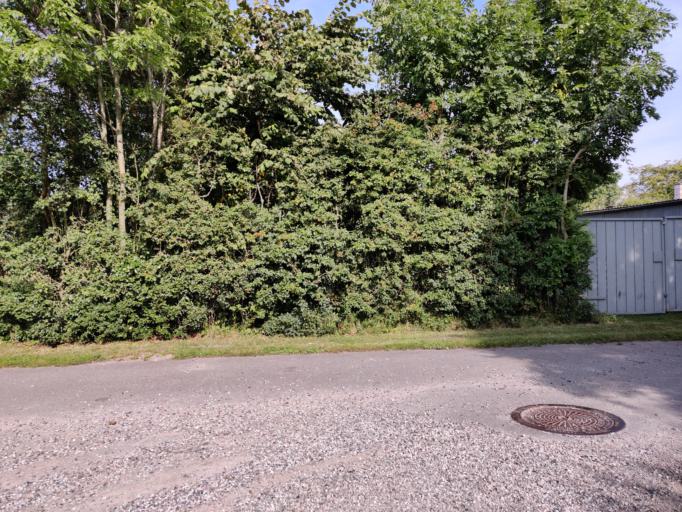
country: DK
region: Zealand
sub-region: Guldborgsund Kommune
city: Nykobing Falster
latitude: 54.6353
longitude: 11.9029
